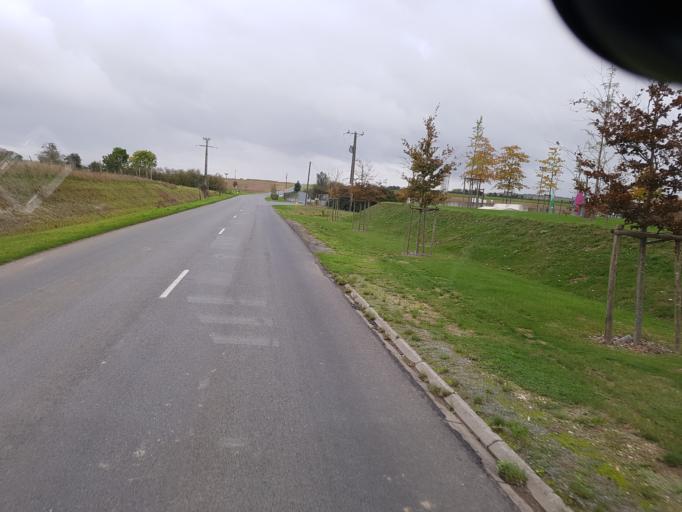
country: FR
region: Nord-Pas-de-Calais
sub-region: Departement du Pas-de-Calais
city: Neuville-Saint-Vaast
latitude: 50.3484
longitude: 2.7466
